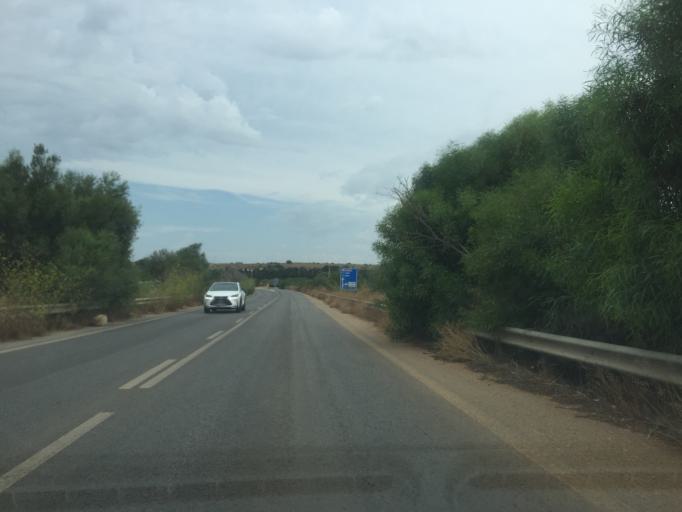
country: IT
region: Sicily
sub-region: Ragusa
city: Donnalucata
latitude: 36.7759
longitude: 14.6152
